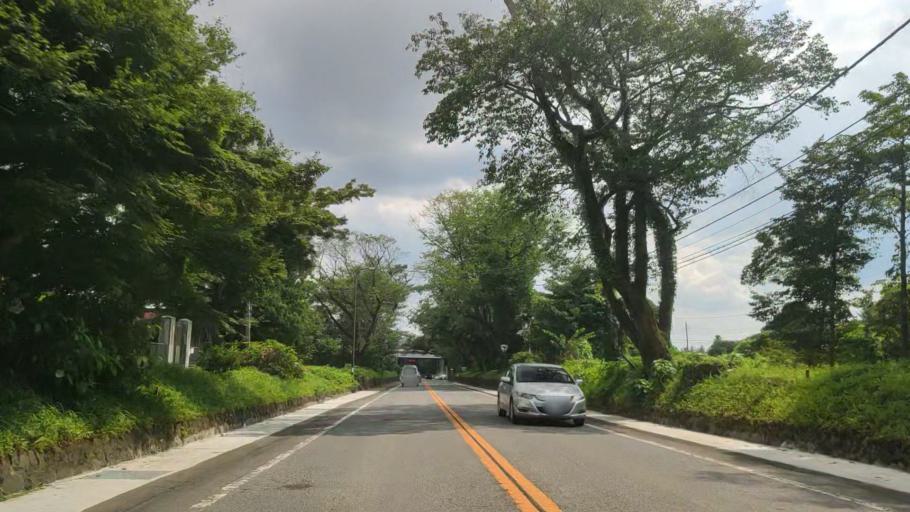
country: JP
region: Tochigi
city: Utsunomiya-shi
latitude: 36.6380
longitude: 139.8491
